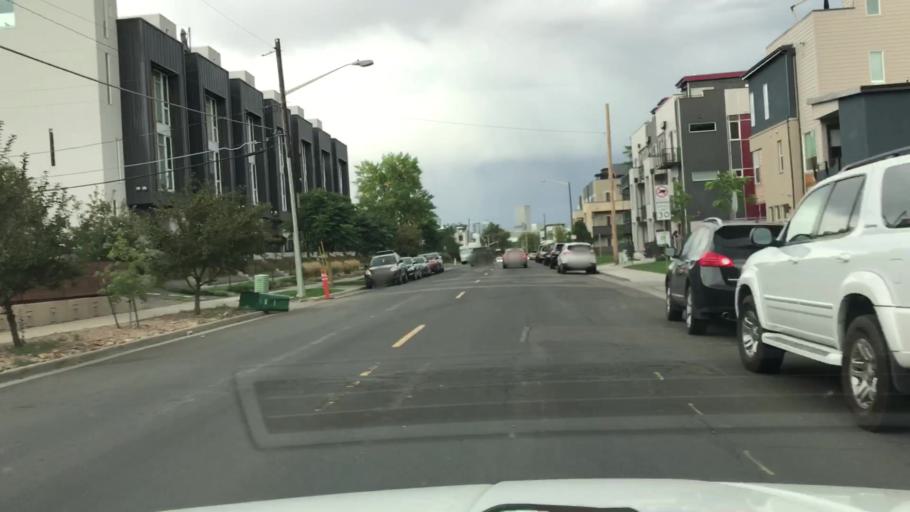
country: US
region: Colorado
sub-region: Jefferson County
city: Edgewater
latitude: 39.7439
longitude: -105.0345
